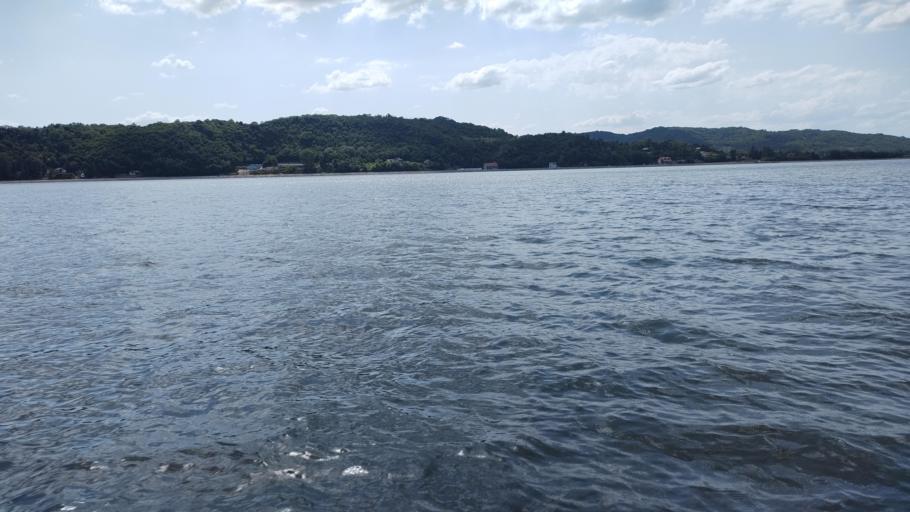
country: RS
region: Central Serbia
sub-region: Branicevski Okrug
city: Golubac
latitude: 44.6625
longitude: 21.6277
